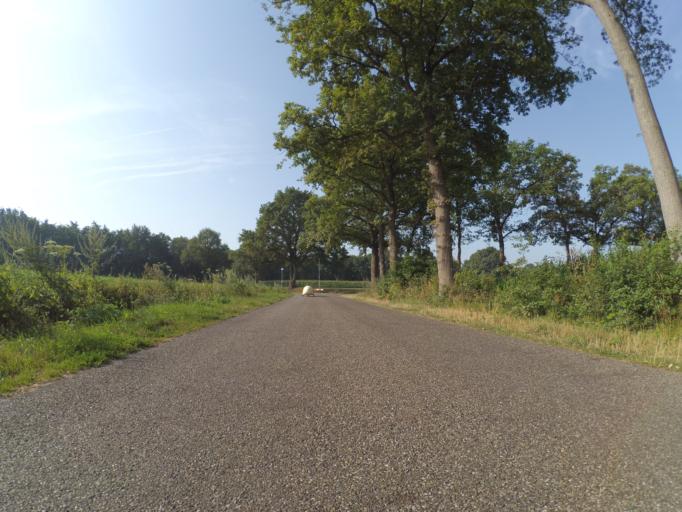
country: NL
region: Overijssel
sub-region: Gemeente Borne
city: Borne
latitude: 52.3389
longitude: 6.7919
